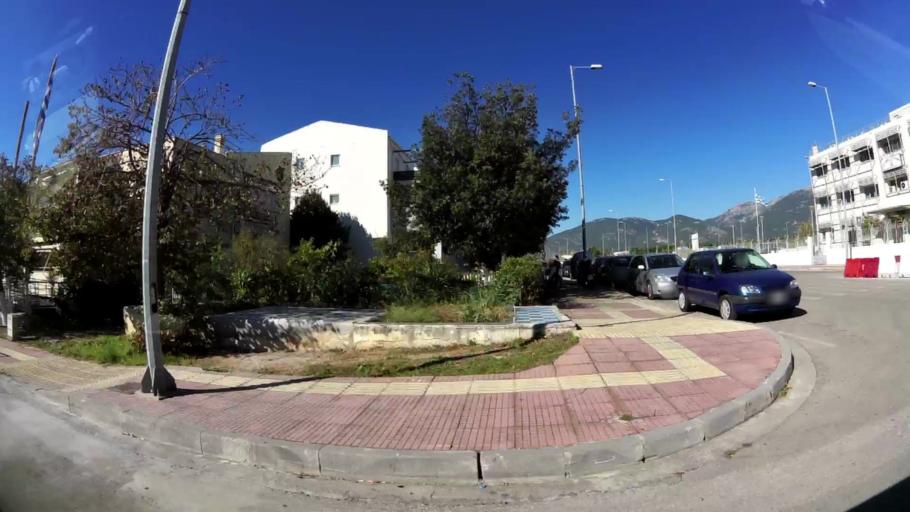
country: GR
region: Attica
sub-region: Nomarchia Anatolikis Attikis
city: Thrakomakedones
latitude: 38.1078
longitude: 23.7674
